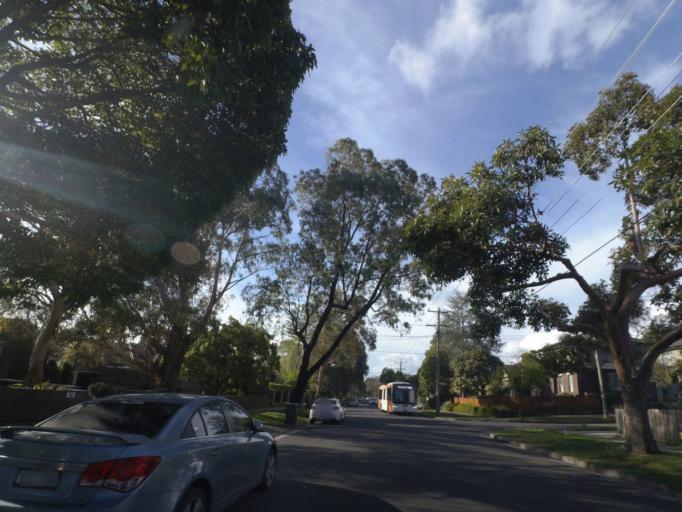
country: AU
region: Victoria
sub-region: Whitehorse
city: Blackburn South
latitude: -37.8302
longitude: 145.1486
